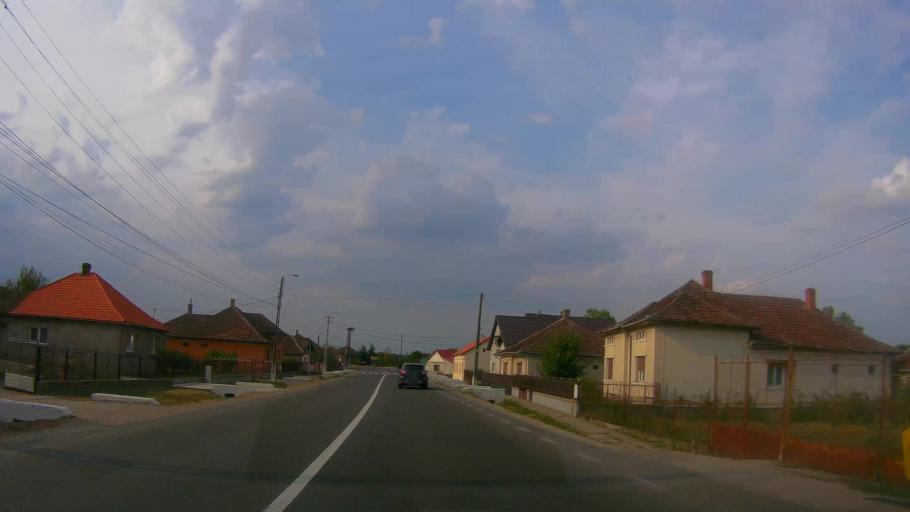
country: RO
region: Satu Mare
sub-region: Oras Ardud
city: Ardud
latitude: 47.6364
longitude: 22.8856
